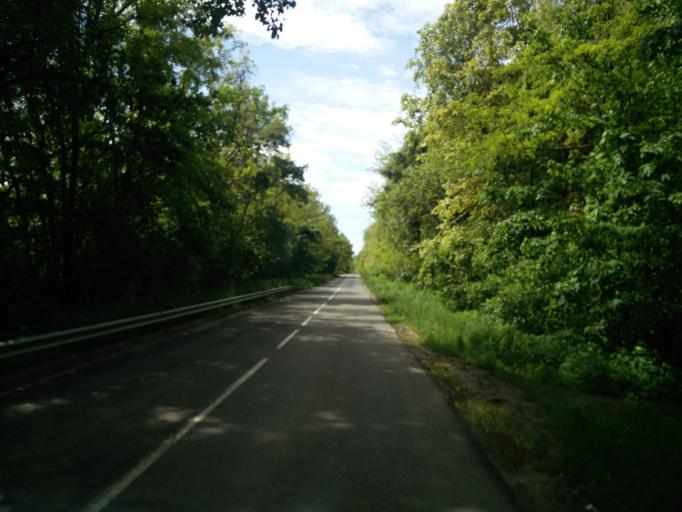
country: HU
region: Tolna
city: Bonyhad
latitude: 46.2631
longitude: 18.6097
